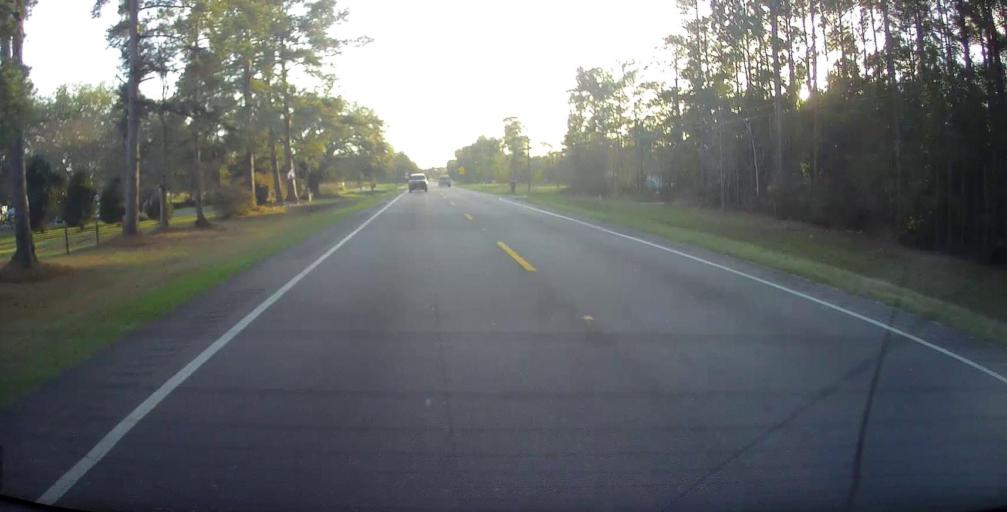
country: US
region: Georgia
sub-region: Effingham County
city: Guyton
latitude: 32.1897
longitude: -81.4472
